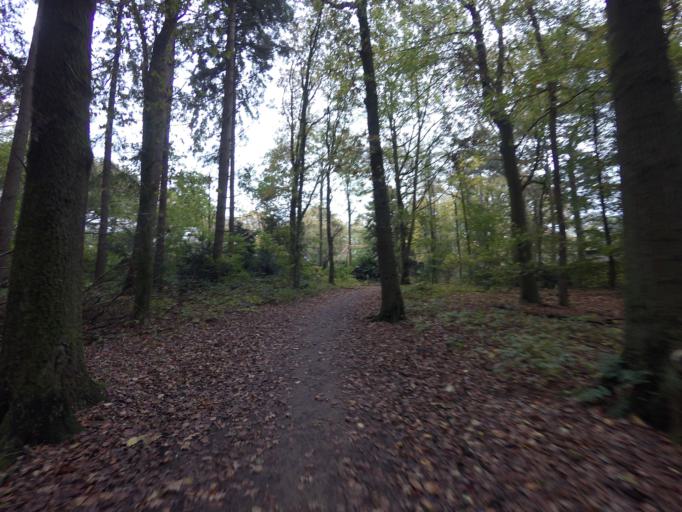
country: NL
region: North Holland
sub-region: Gemeente Hilversum
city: Hilversum
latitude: 52.2045
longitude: 5.1735
